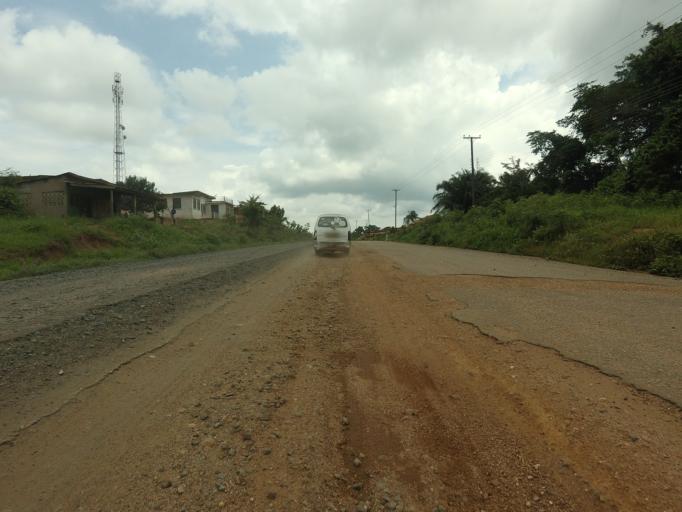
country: GH
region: Volta
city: Ho
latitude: 6.6250
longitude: 0.3103
